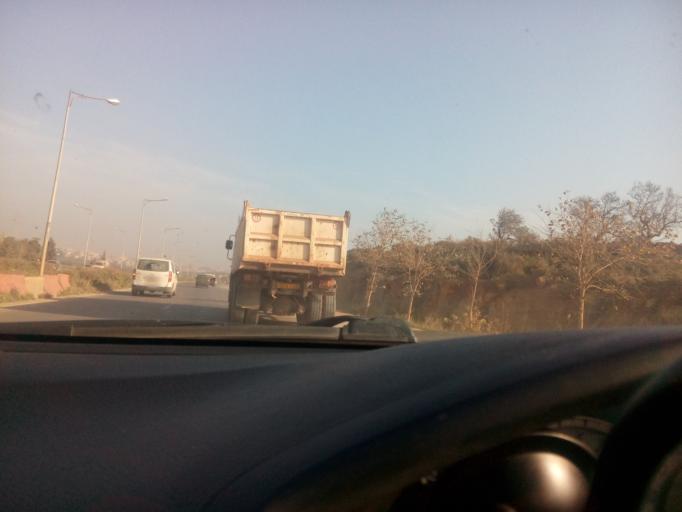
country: DZ
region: Oran
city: Es Senia
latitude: 35.6497
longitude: -0.6717
